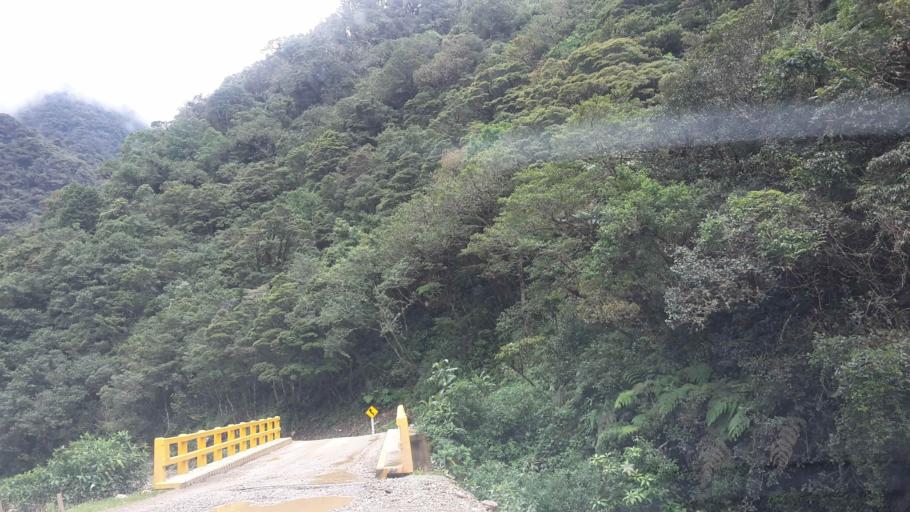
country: BO
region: Cochabamba
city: Totora
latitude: -17.5436
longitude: -65.2688
